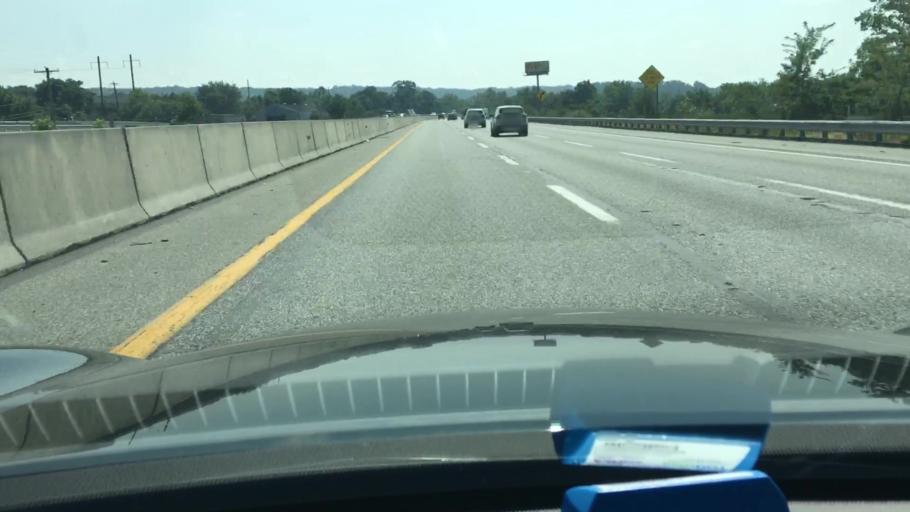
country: US
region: Pennsylvania
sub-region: Montgomery County
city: Bridgeport
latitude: 40.0923
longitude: -75.3472
